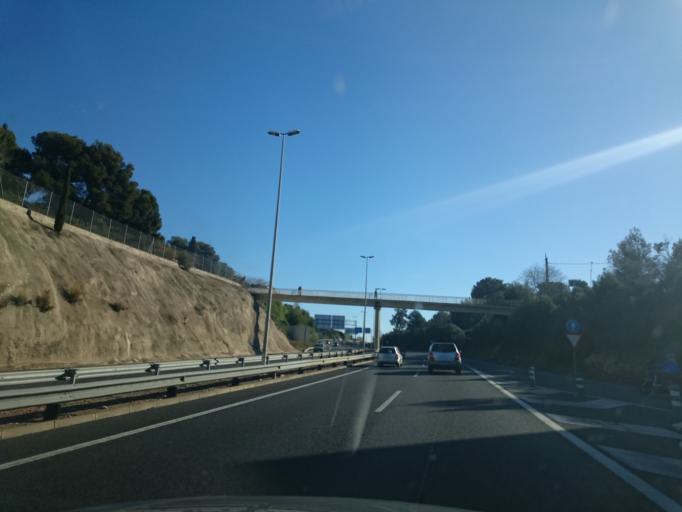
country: ES
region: Catalonia
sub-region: Provincia de Tarragona
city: Tarragona
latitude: 41.1248
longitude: 1.2460
